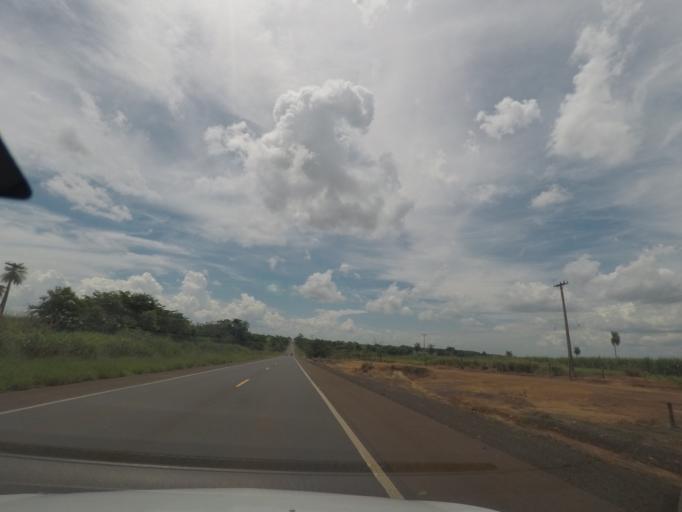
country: BR
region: Sao Paulo
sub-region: Barretos
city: Barretos
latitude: -20.3724
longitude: -48.6451
